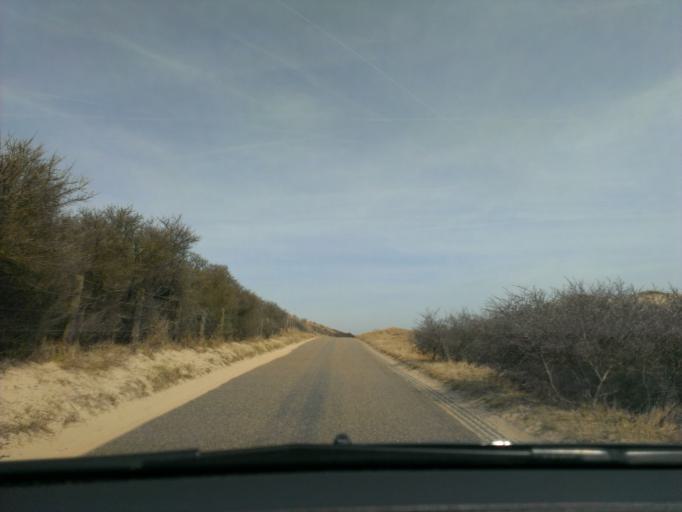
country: NL
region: North Holland
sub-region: Gemeente Zandvoort
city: Zandvoort
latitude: 52.4102
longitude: 4.5500
